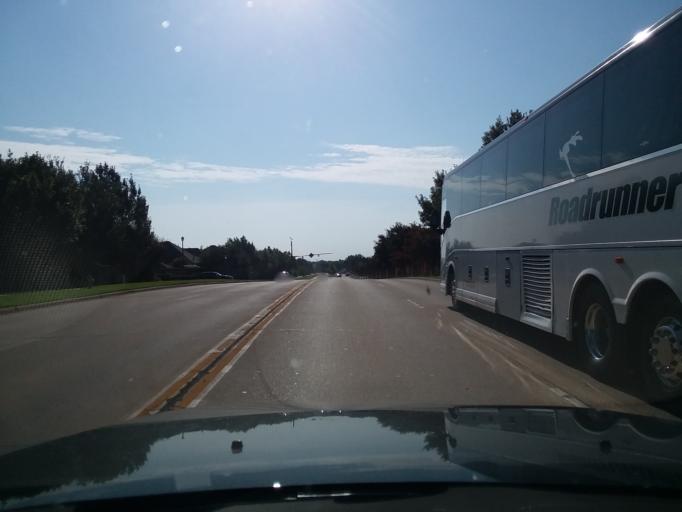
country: US
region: Texas
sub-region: Denton County
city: Highland Village
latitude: 33.0663
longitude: -97.0587
